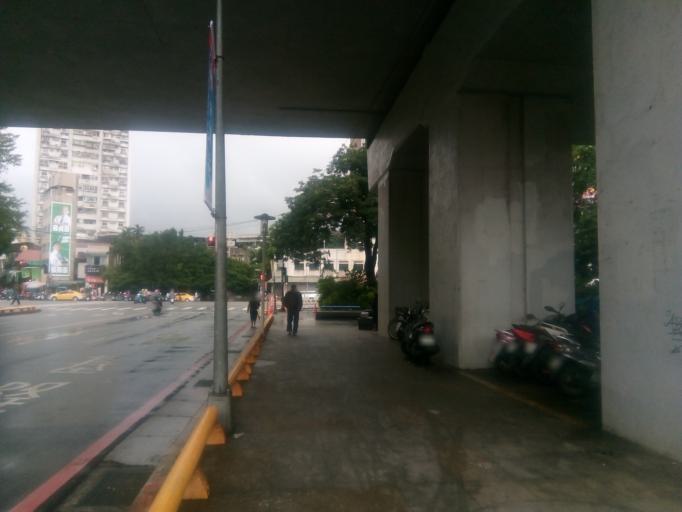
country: TW
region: Taiwan
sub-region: Keelung
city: Keelung
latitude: 25.0692
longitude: 121.6628
